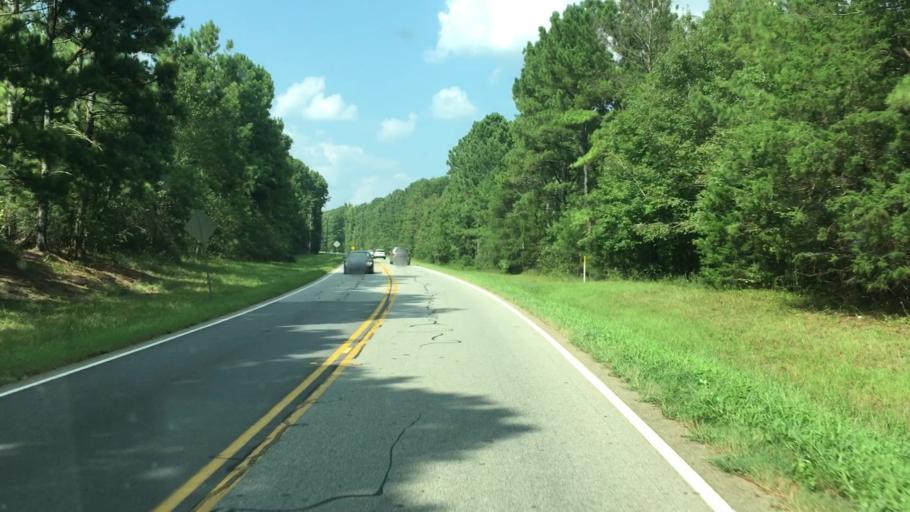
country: US
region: Georgia
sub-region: Jasper County
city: Monticello
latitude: 33.2730
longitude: -83.7142
